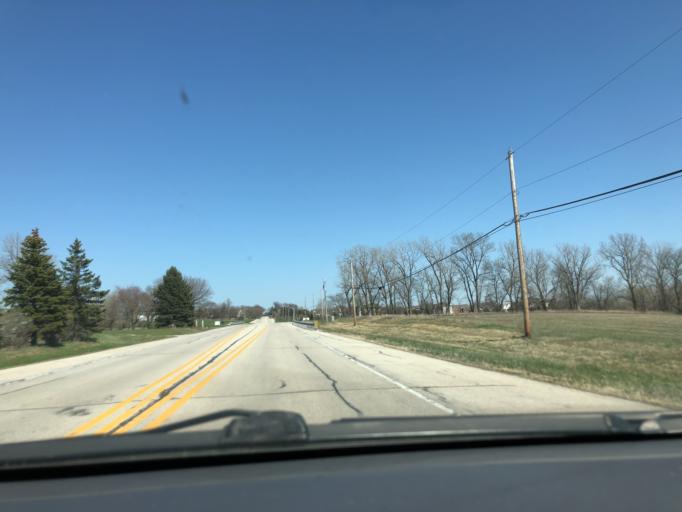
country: US
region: Illinois
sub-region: Kane County
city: Hampshire
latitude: 42.1609
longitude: -88.5088
